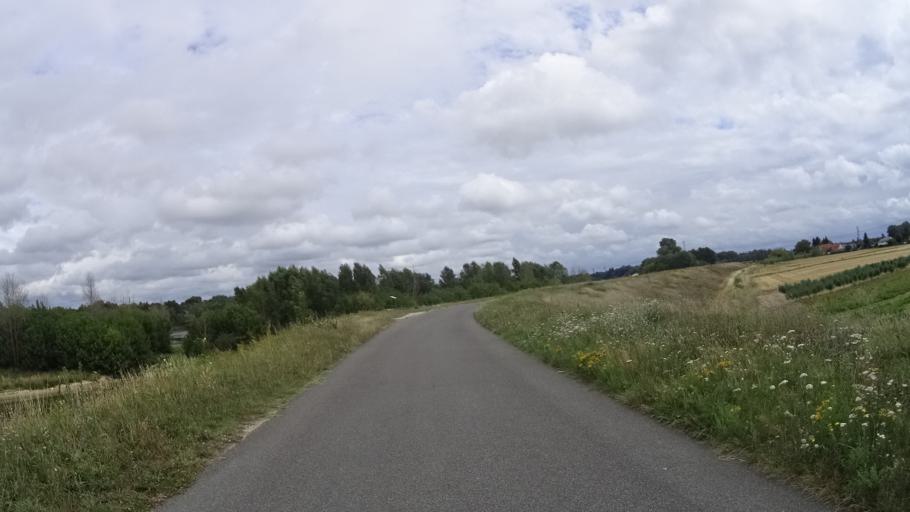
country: FR
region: Centre
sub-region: Departement du Loiret
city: Mareau-aux-Pres
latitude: 47.8635
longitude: 1.7846
